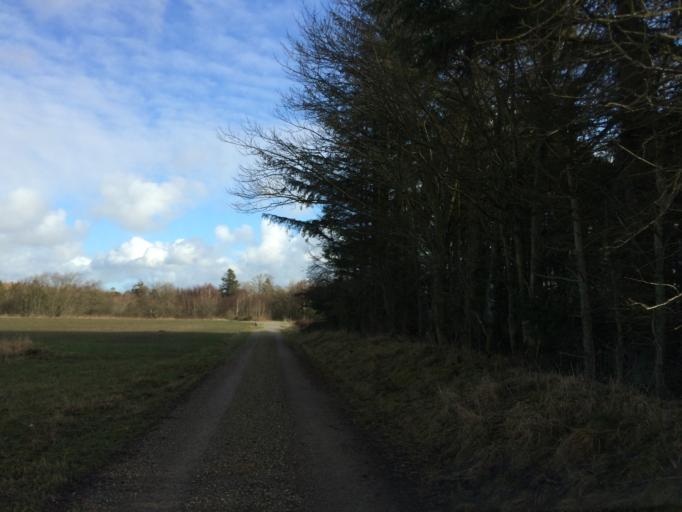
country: DK
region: Central Jutland
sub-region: Holstebro Kommune
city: Ulfborg
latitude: 56.2703
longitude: 8.3305
